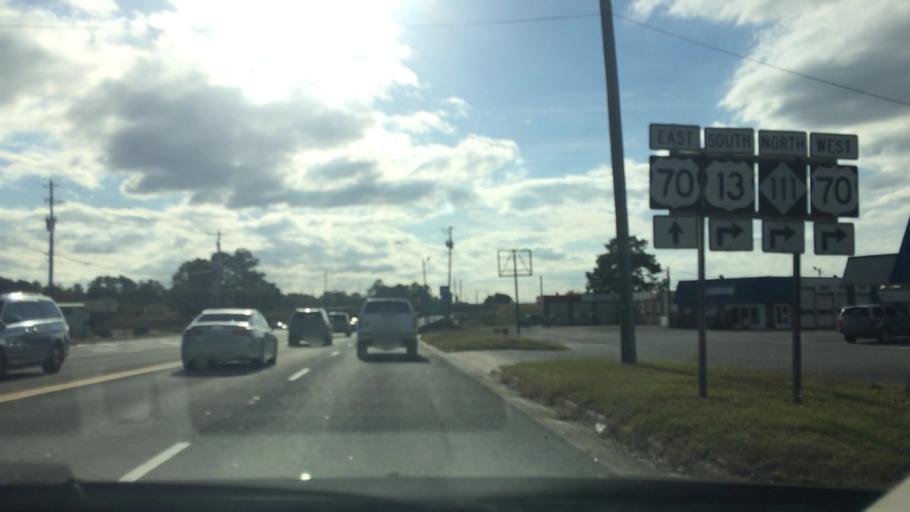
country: US
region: North Carolina
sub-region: Wayne County
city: Elroy
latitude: 35.3796
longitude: -77.9344
